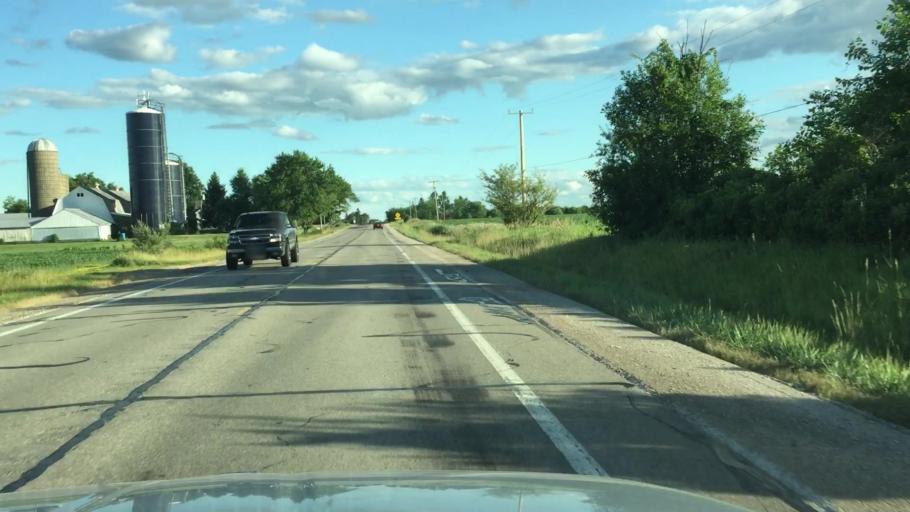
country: US
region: Michigan
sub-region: Saint Clair County
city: Yale
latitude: 43.0915
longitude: -82.7663
